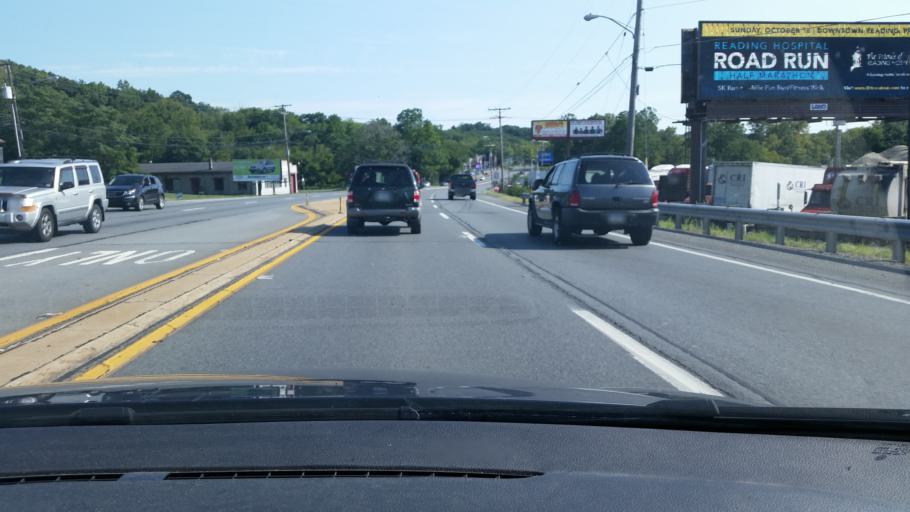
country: US
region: Pennsylvania
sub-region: Berks County
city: Hamburg
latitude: 40.5415
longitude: -75.9780
